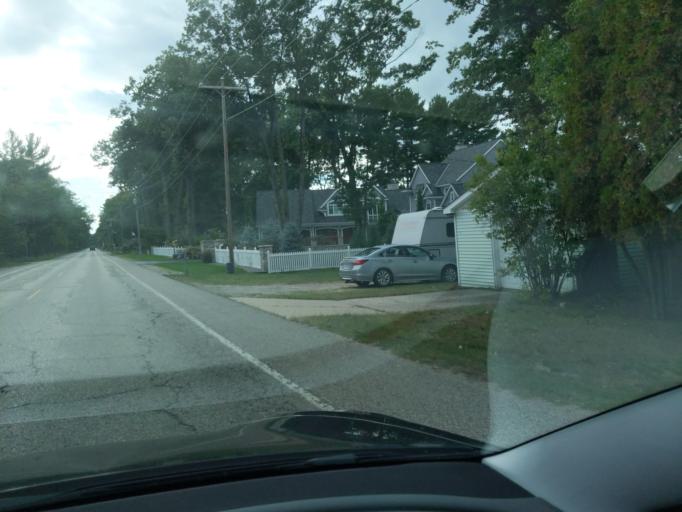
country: US
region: Michigan
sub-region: Kalkaska County
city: Rapid City
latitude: 44.8588
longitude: -85.2919
